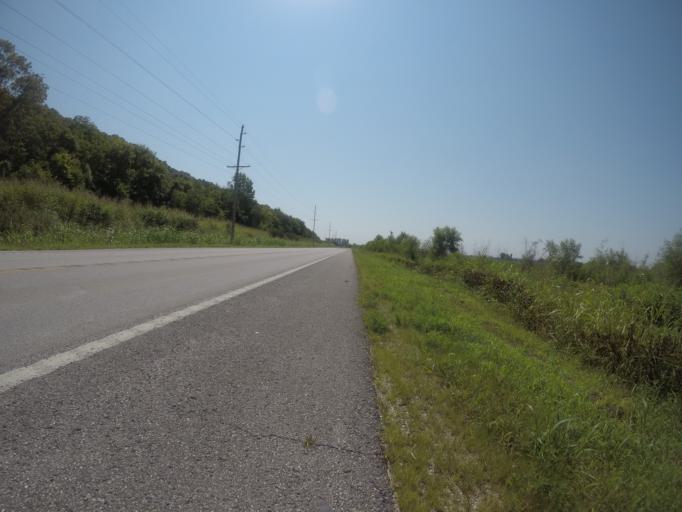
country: US
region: Kansas
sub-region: Atchison County
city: Atchison
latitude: 39.5379
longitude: -95.0403
